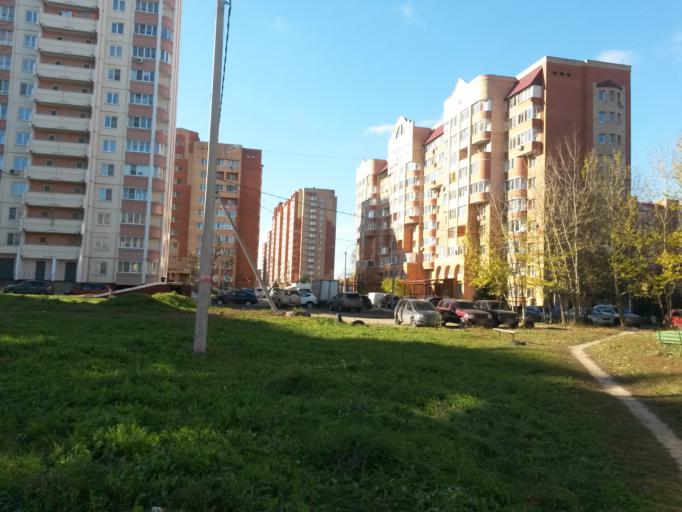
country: RU
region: Moskovskaya
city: Domodedovo
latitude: 55.4258
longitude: 37.7620
